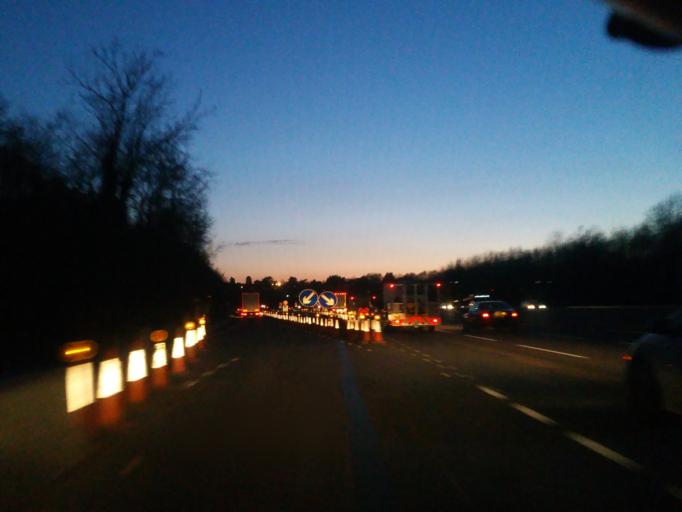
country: GB
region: England
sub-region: Surrey
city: Bagshot
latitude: 51.3583
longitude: -0.6721
